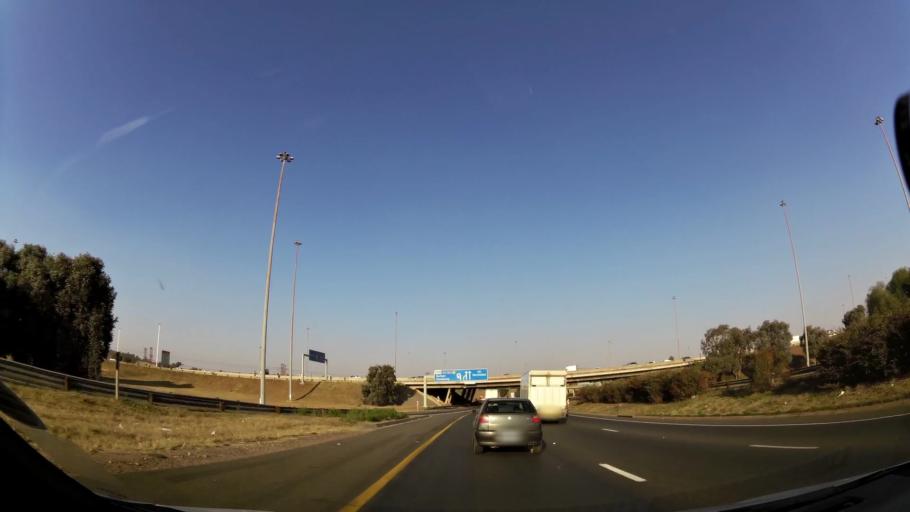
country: ZA
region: Gauteng
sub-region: Ekurhuleni Metropolitan Municipality
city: Germiston
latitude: -26.2116
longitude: 28.1334
